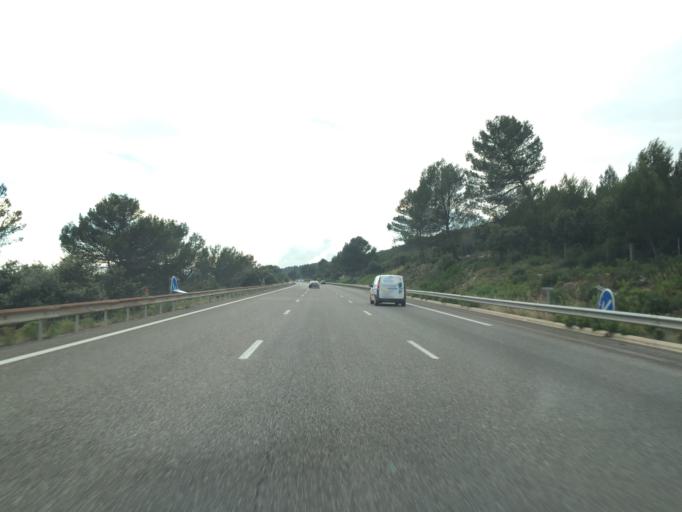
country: FR
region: Provence-Alpes-Cote d'Azur
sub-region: Departement du Var
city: La Celle
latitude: 43.4203
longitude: 6.0162
